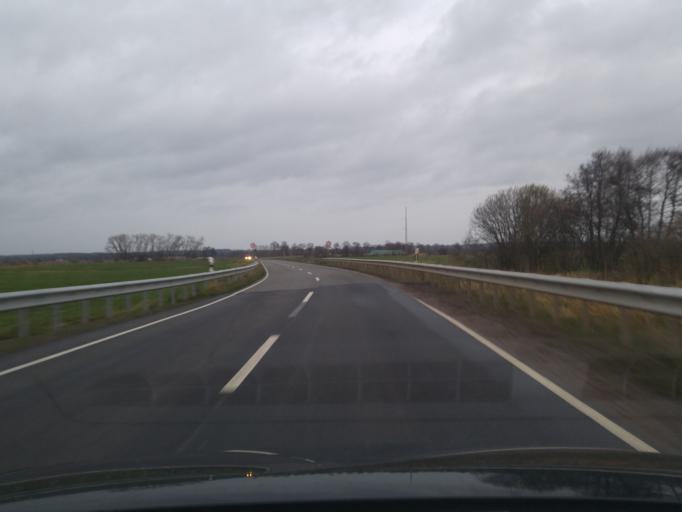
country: DE
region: Lower Saxony
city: Echem
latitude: 53.3326
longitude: 10.5156
